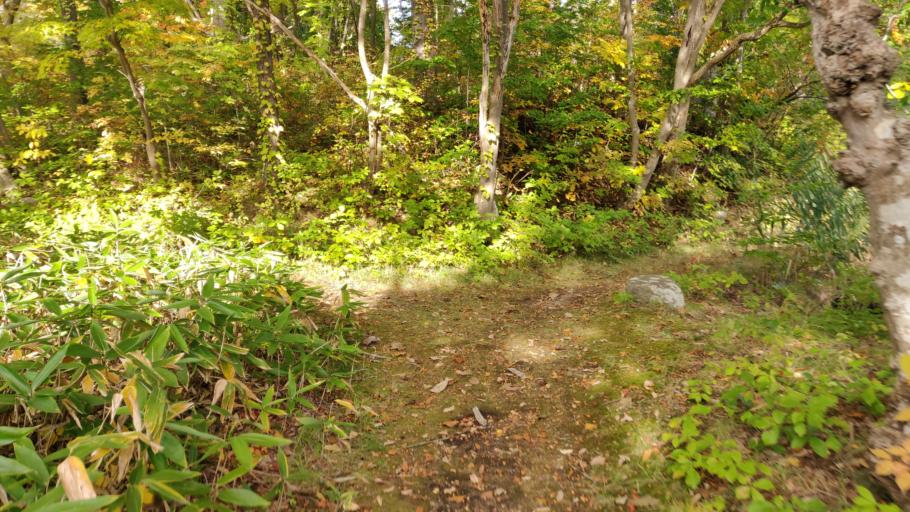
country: JP
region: Hokkaido
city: Nanae
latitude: 41.9844
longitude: 140.6672
